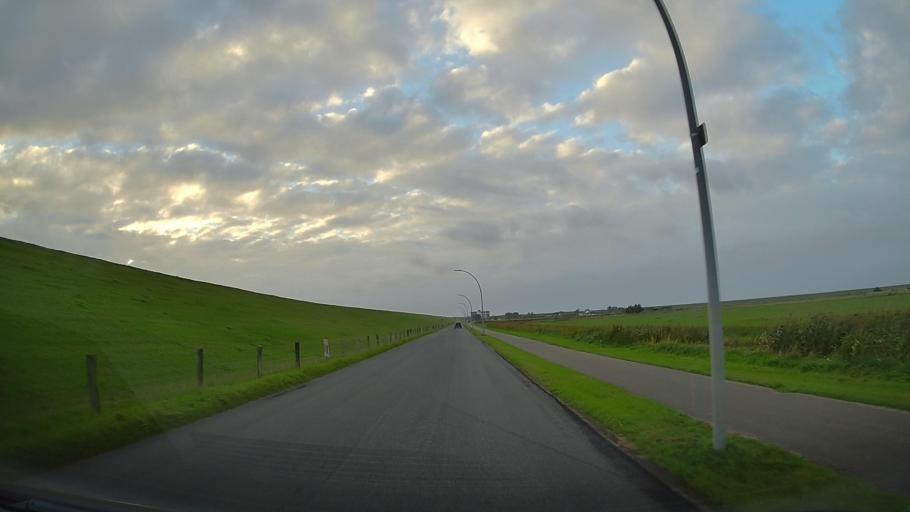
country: DE
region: Schleswig-Holstein
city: Husum
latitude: 54.4745
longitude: 9.0223
